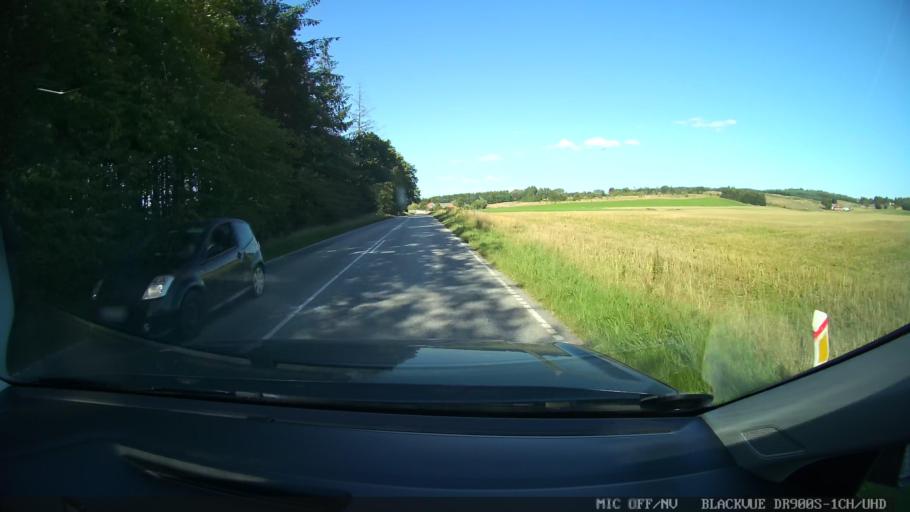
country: DK
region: North Denmark
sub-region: Mariagerfjord Kommune
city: Mariager
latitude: 56.6350
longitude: 9.9777
